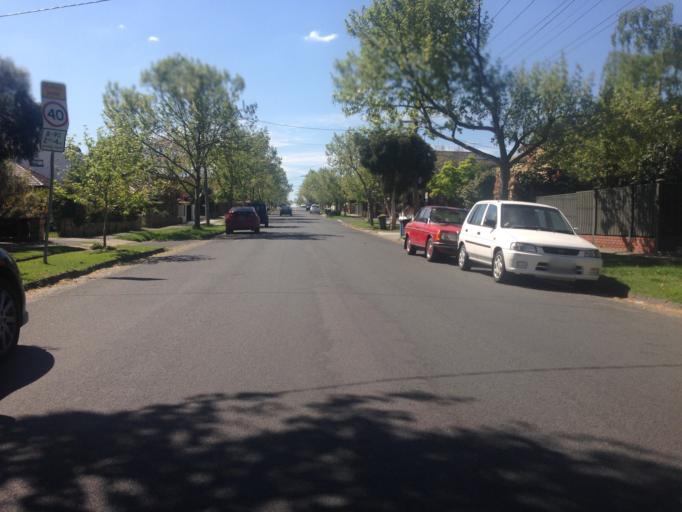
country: AU
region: Victoria
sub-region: Boroondara
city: Kew East
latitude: -37.7971
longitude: 145.0472
